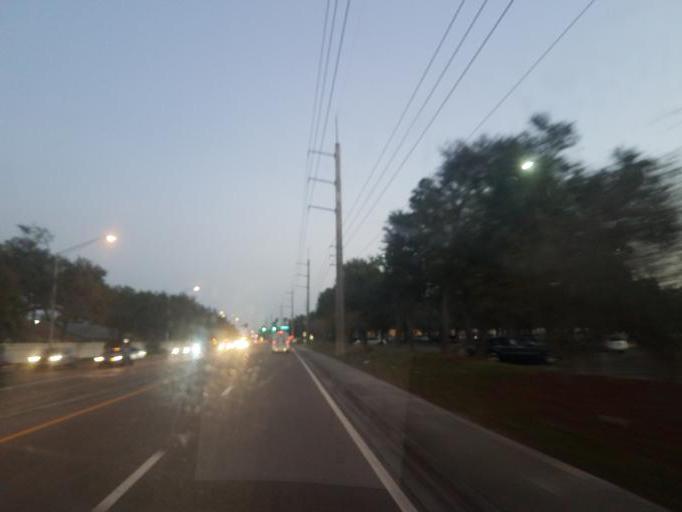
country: US
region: Florida
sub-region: Sarasota County
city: Lake Sarasota
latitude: 27.2934
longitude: -82.4518
